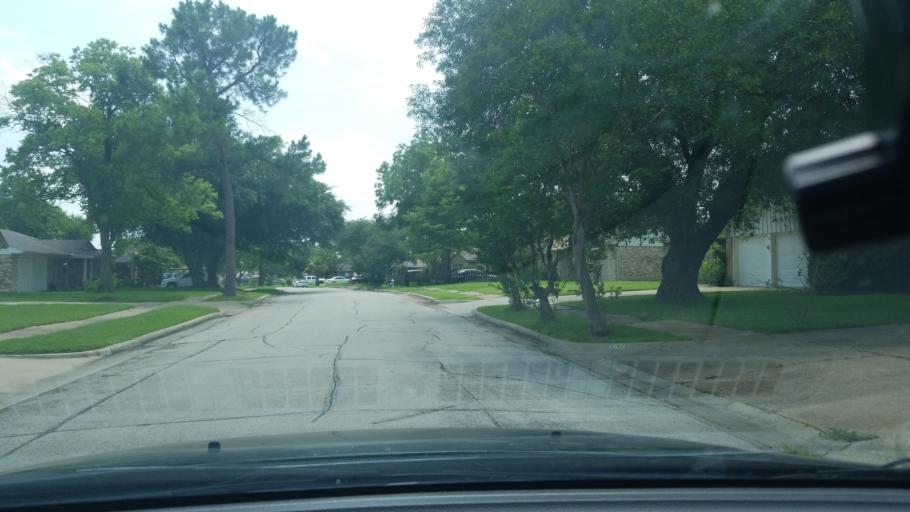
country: US
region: Texas
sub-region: Dallas County
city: Mesquite
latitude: 32.8017
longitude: -96.6398
